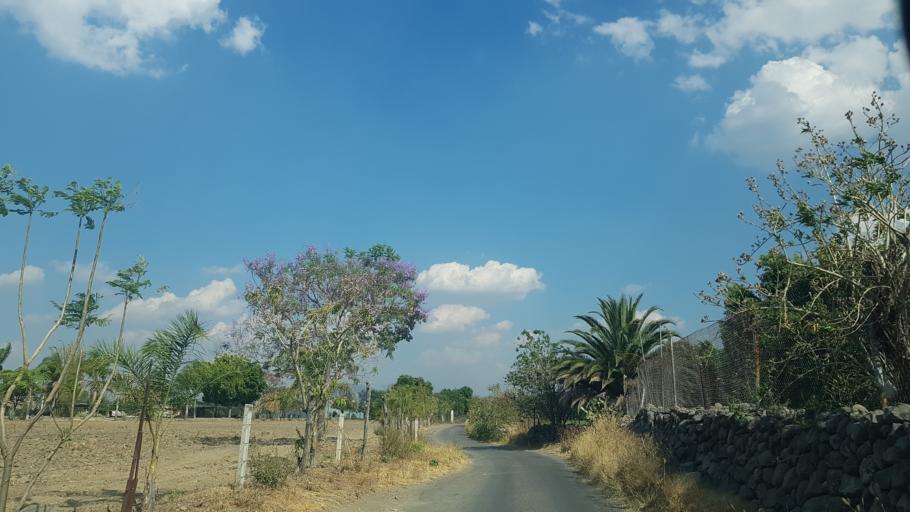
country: MX
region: Puebla
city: Atlixco
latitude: 18.8807
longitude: -98.4871
